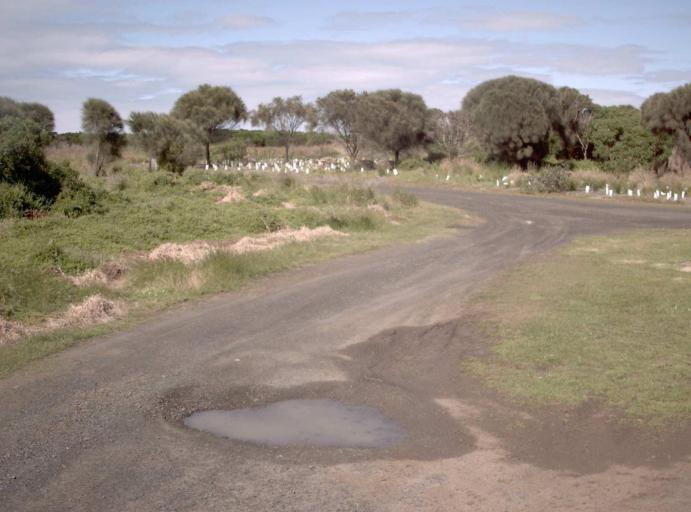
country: AU
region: Victoria
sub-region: Bass Coast
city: Phillip Island
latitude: -38.5065
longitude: 145.1433
